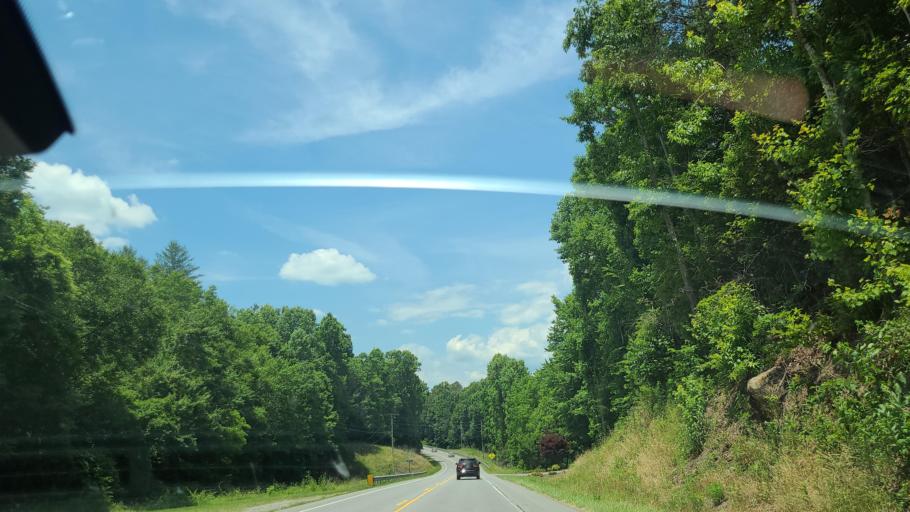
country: US
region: North Carolina
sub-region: Clay County
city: Hayesville
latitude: 35.0532
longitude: -83.9135
